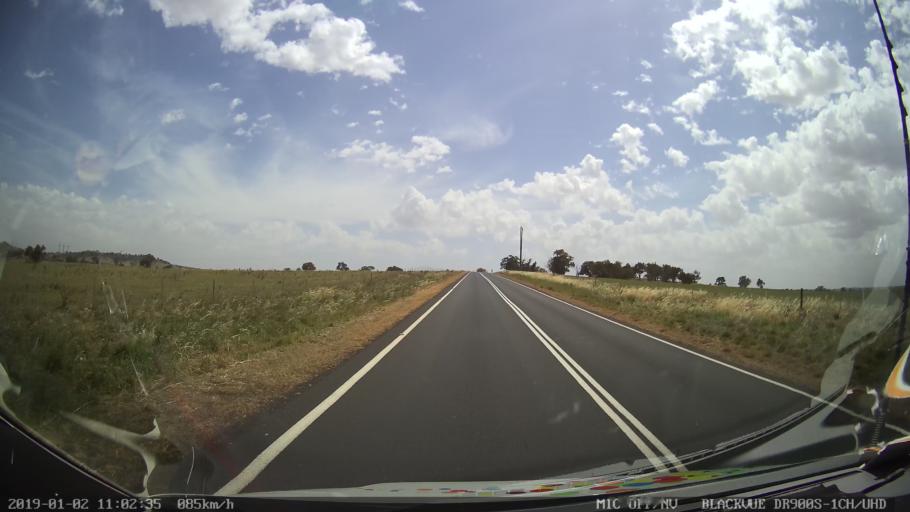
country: AU
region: New South Wales
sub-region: Young
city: Young
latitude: -34.5843
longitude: 148.3282
